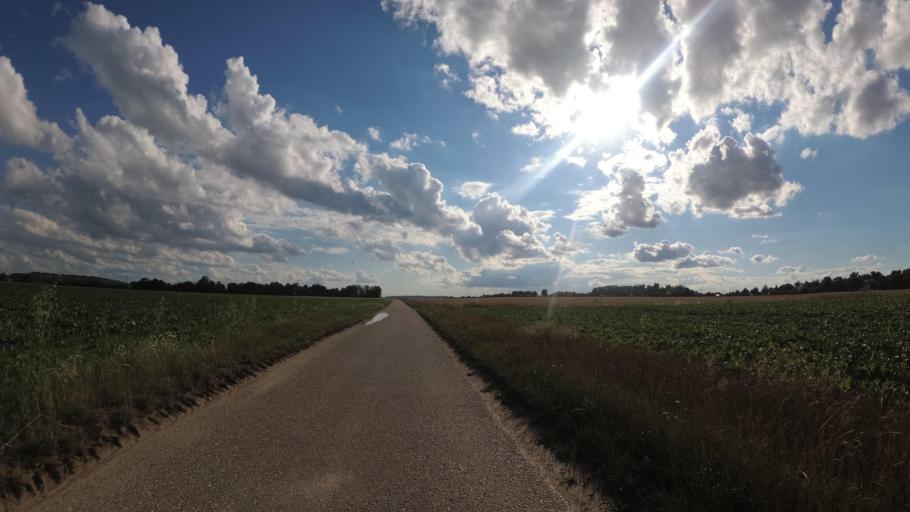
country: DE
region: Baden-Wuerttemberg
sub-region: Regierungsbezirk Stuttgart
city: Oedheim
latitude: 49.2334
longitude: 9.2590
